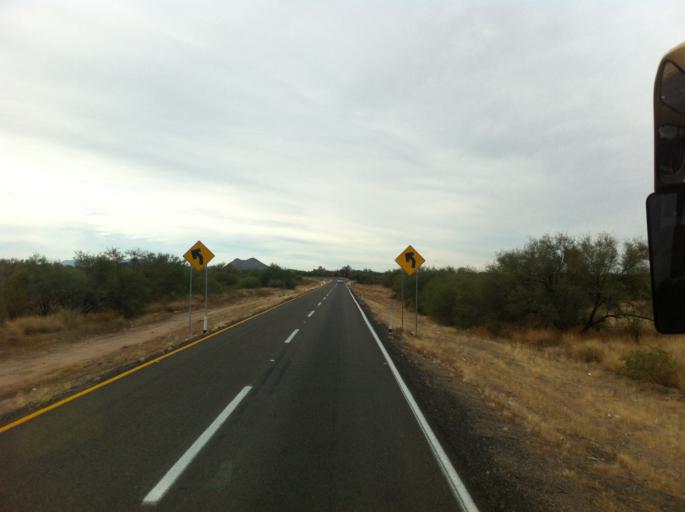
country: MX
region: Sonora
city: Hermosillo
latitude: 28.8742
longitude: -110.9595
